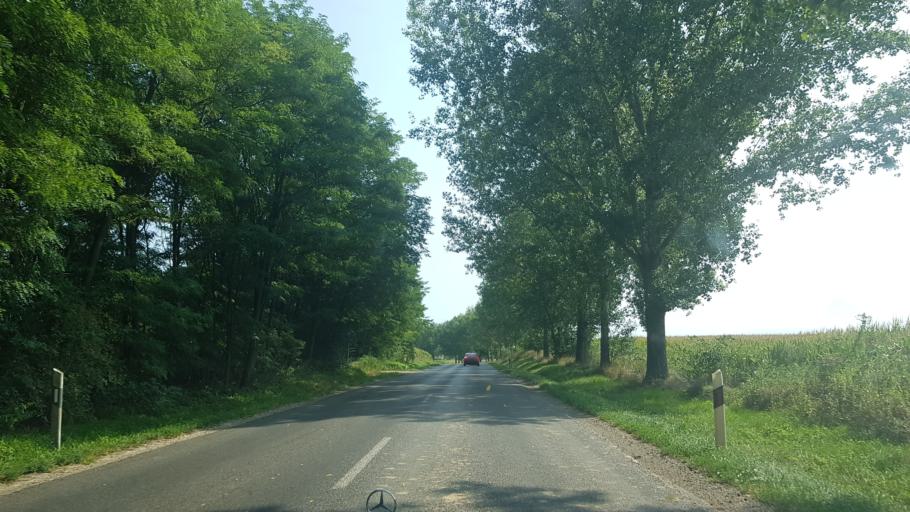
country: HU
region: Somogy
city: Segesd
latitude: 46.3617
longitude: 17.3475
